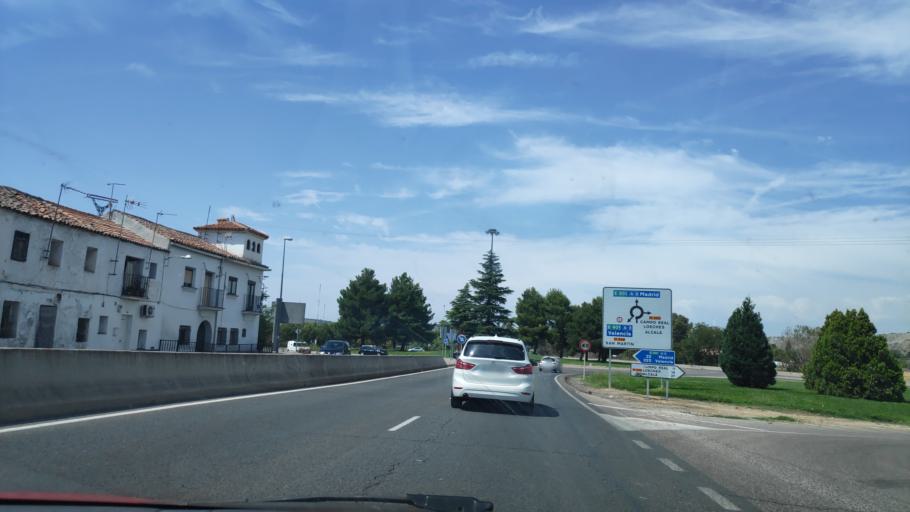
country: ES
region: Madrid
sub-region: Provincia de Madrid
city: Vaciamadrid
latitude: 40.3118
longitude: -3.4874
